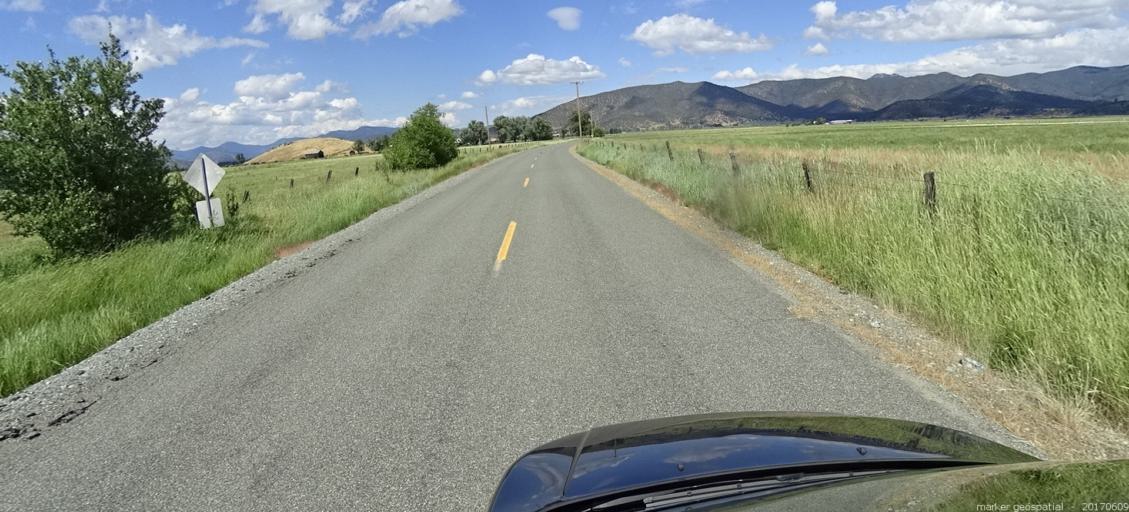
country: US
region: California
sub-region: Siskiyou County
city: Yreka
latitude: 41.4851
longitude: -122.8760
